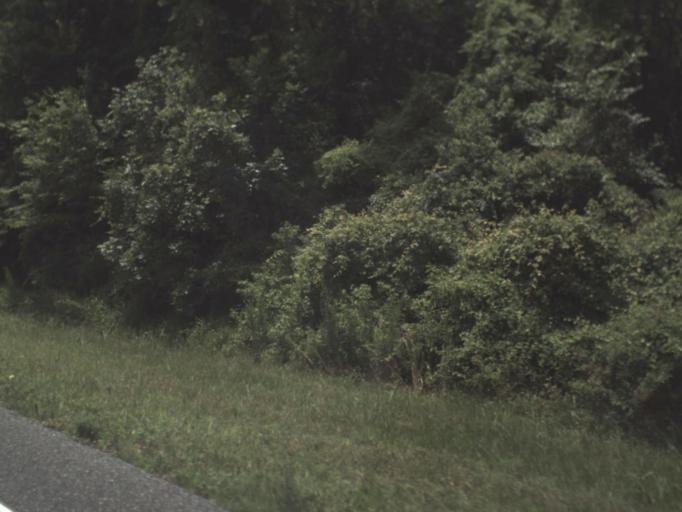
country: US
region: Florida
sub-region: Taylor County
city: Perry
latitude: 29.9293
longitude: -83.4433
